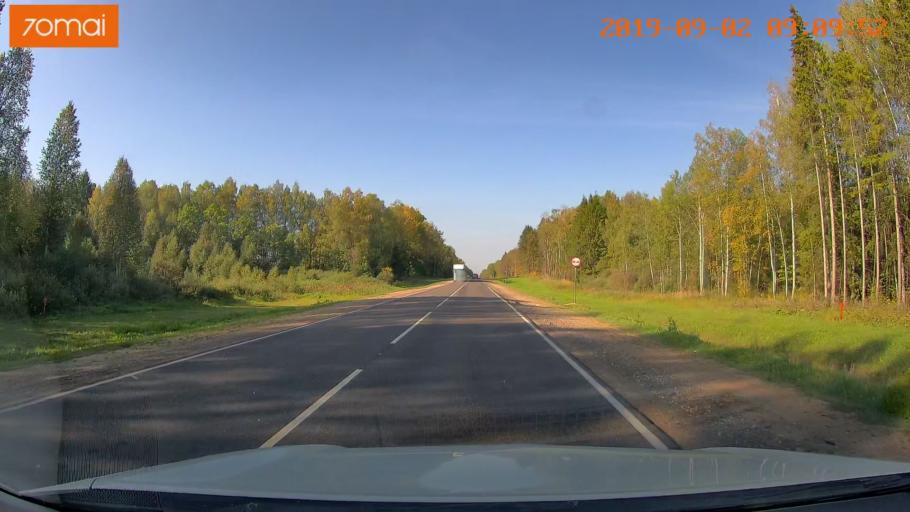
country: RU
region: Kaluga
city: Myatlevo
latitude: 54.8809
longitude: 35.6145
